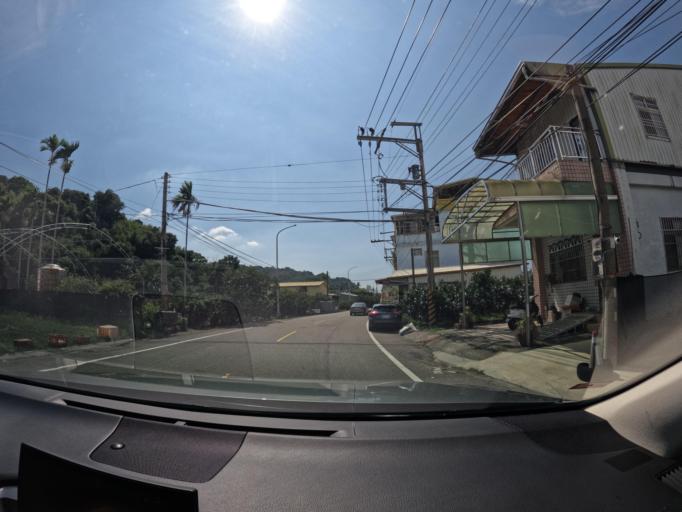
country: TW
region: Taiwan
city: Fengyuan
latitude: 24.3111
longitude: 120.7881
